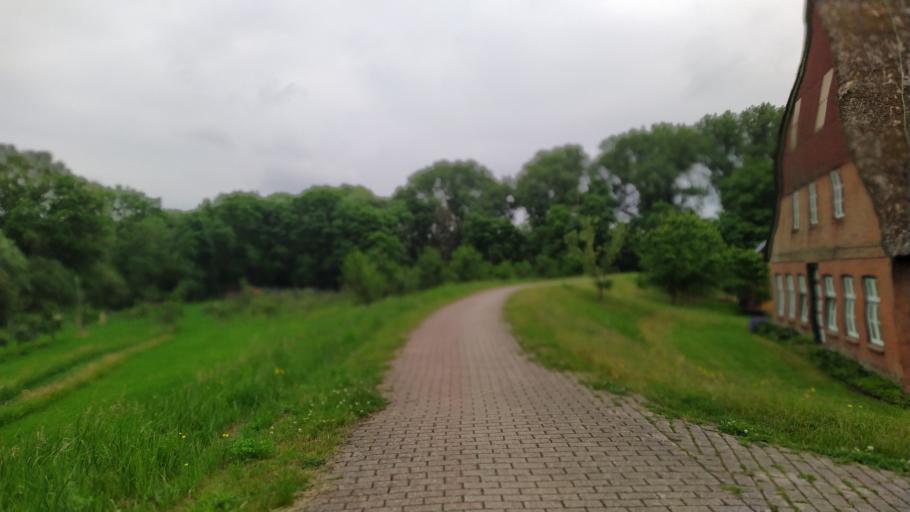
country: DE
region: Hamburg
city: Altona
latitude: 53.4998
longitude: 9.8981
